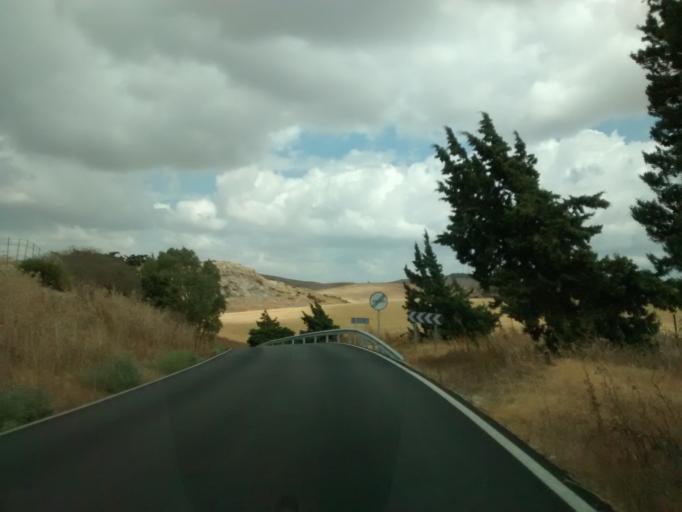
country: ES
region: Andalusia
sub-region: Provincia de Cadiz
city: Paterna de Rivera
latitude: 36.5056
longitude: -5.8809
